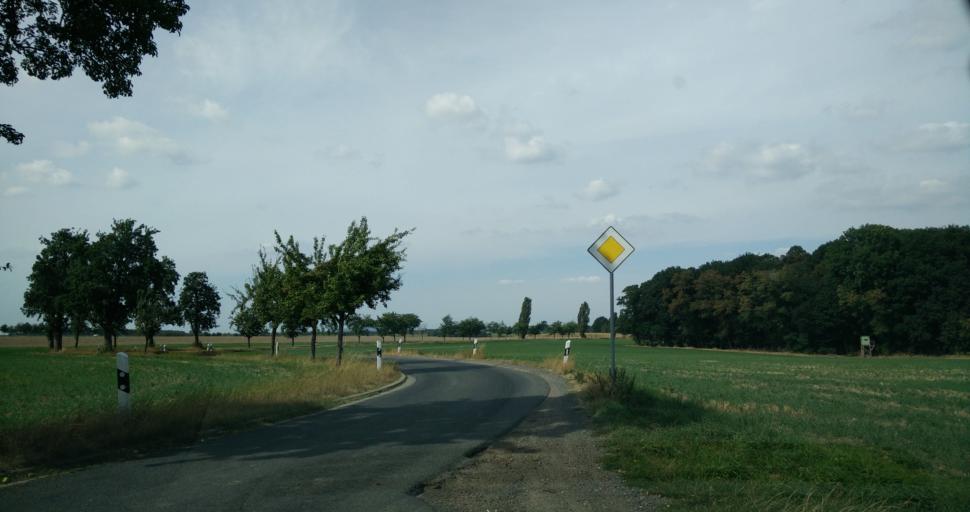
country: DE
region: Saxony
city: Bad Lausick
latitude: 51.1119
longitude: 12.6888
